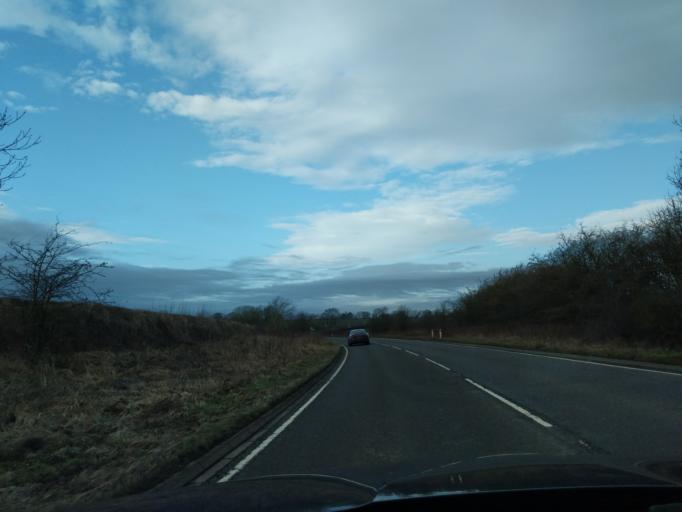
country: GB
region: England
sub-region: Northumberland
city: Meldon
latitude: 55.0777
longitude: -1.8008
